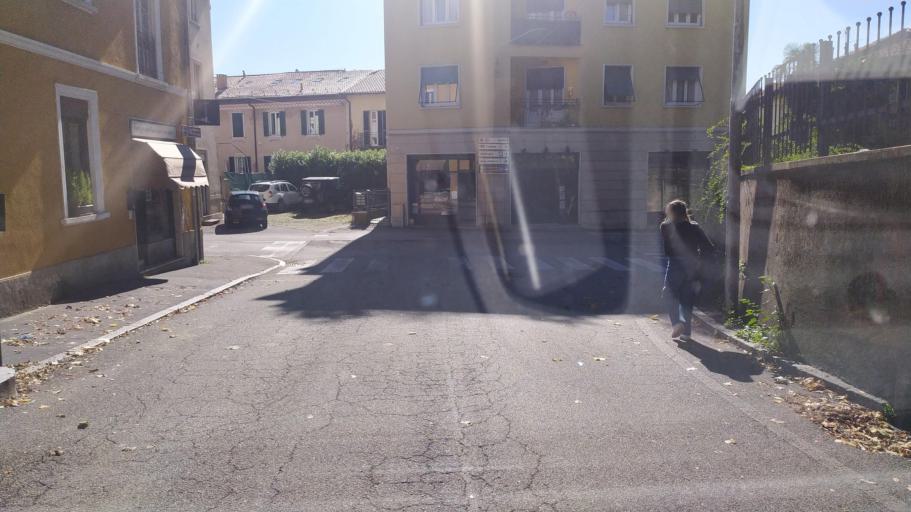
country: IT
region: Lombardy
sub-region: Provincia di Varese
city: Varese
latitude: 45.8156
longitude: 8.8135
